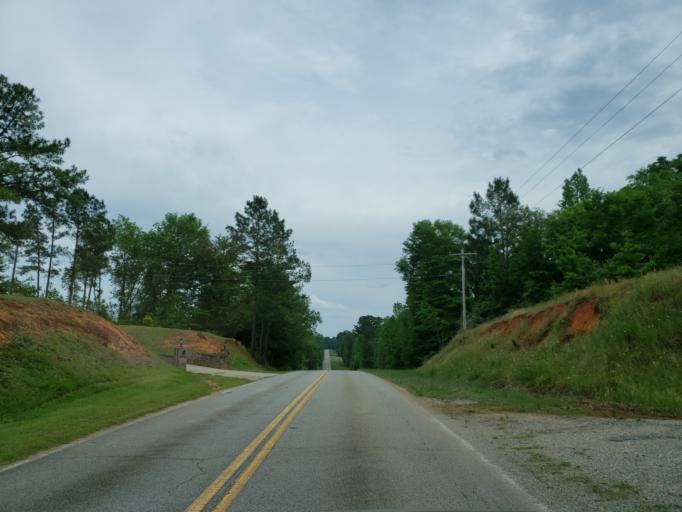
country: US
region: Georgia
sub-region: Bibb County
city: West Point
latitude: 32.8250
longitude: -83.8766
